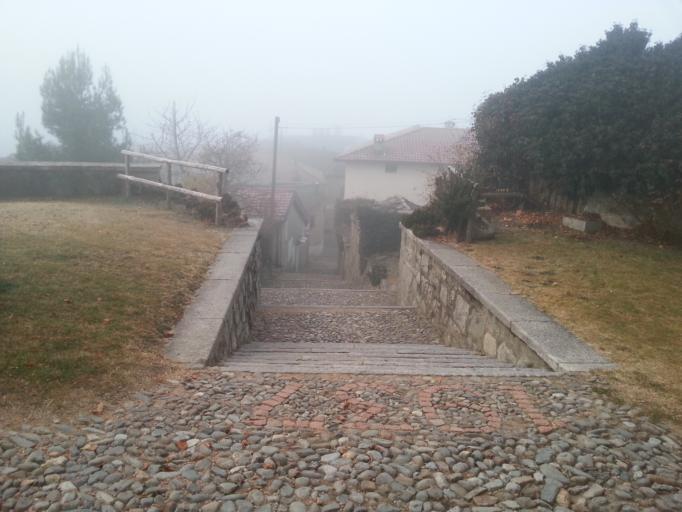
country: CH
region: Ticino
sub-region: Lugano District
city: Agno
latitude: 46.0331
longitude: 8.8703
